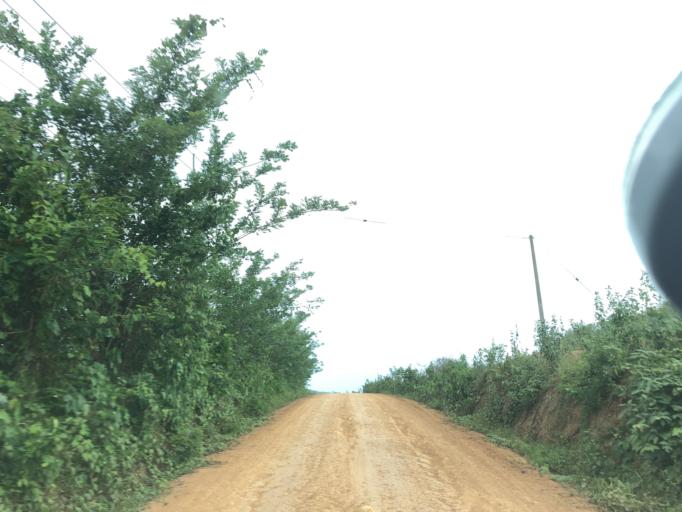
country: TH
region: Loei
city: Chiang Khan
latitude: 17.9965
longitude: 101.4190
